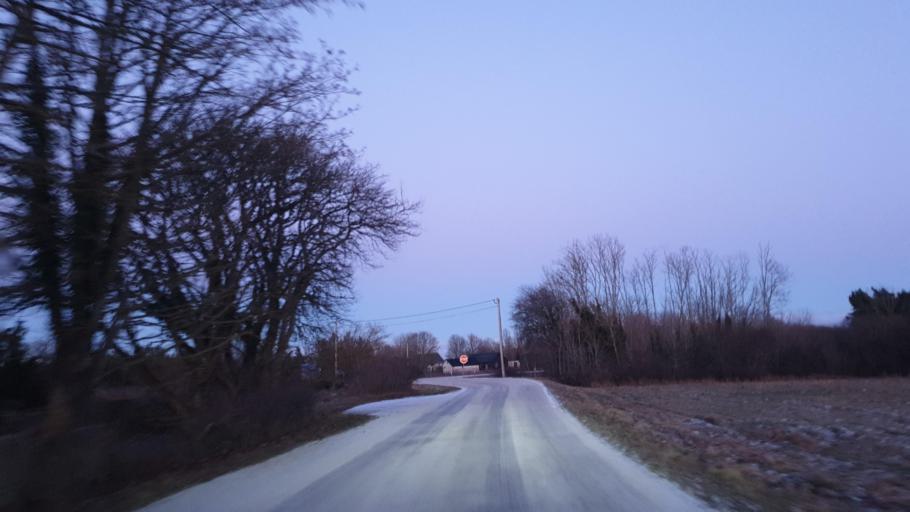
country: SE
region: Gotland
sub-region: Gotland
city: Slite
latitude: 57.4253
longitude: 18.8324
